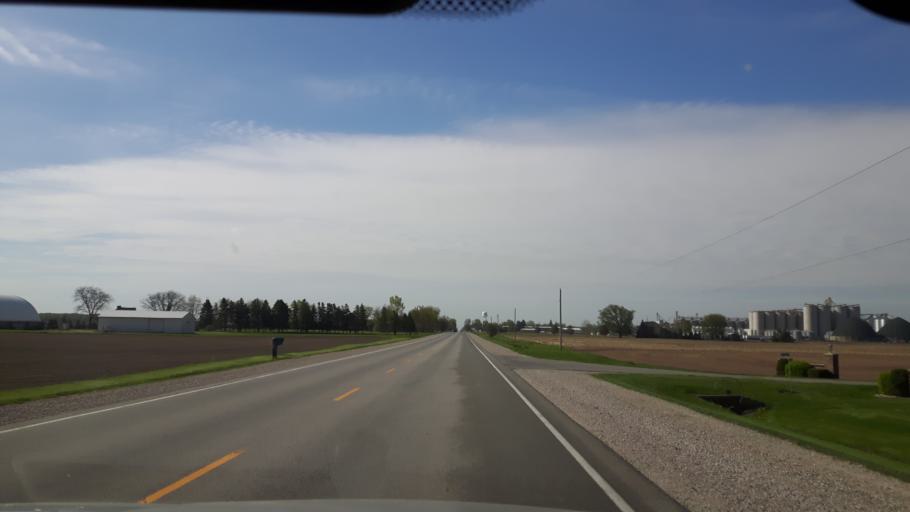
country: CA
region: Ontario
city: Bluewater
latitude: 43.4484
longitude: -81.5015
